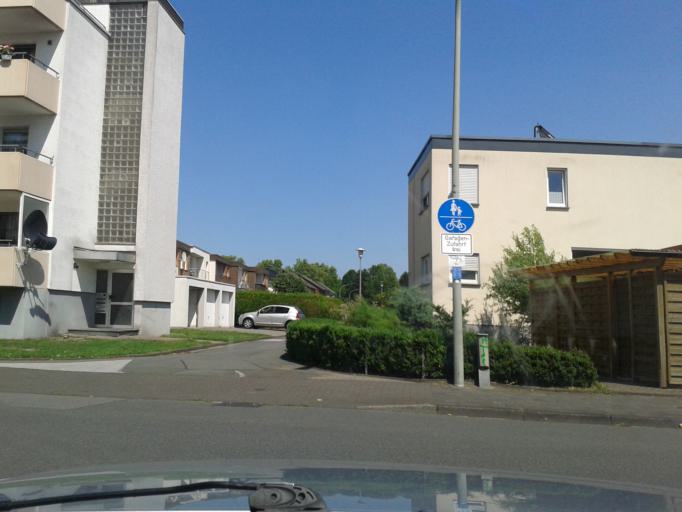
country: DE
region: North Rhine-Westphalia
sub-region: Regierungsbezirk Detmold
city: Paderborn
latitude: 51.7412
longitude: 8.7573
